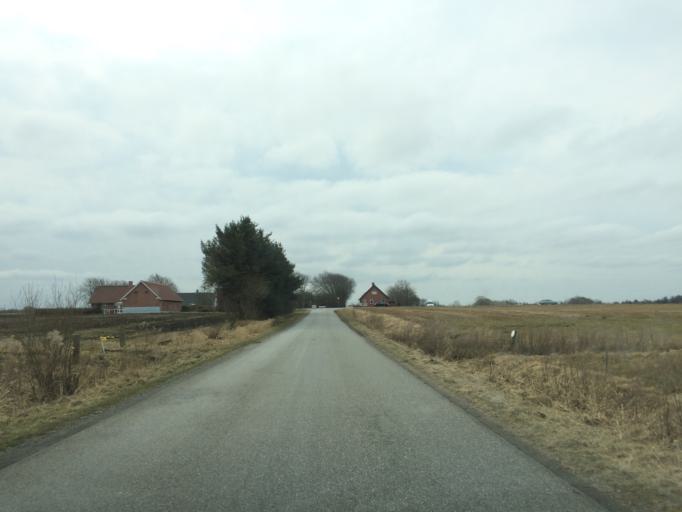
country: DK
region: South Denmark
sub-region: Varde Kommune
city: Oksbol
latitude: 55.7926
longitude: 8.3585
